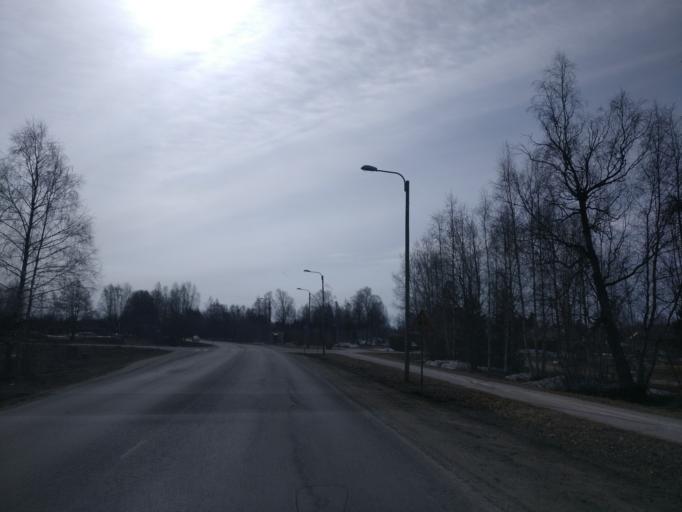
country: FI
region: Lapland
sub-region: Kemi-Tornio
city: Kemi
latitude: 65.7557
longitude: 24.5495
